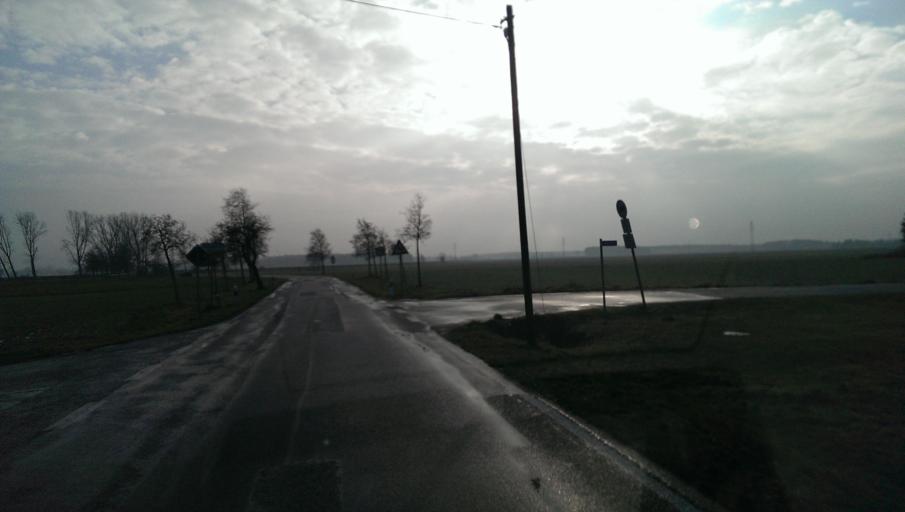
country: DE
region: Saxony
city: Nauwalde
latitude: 51.4563
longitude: 13.4266
